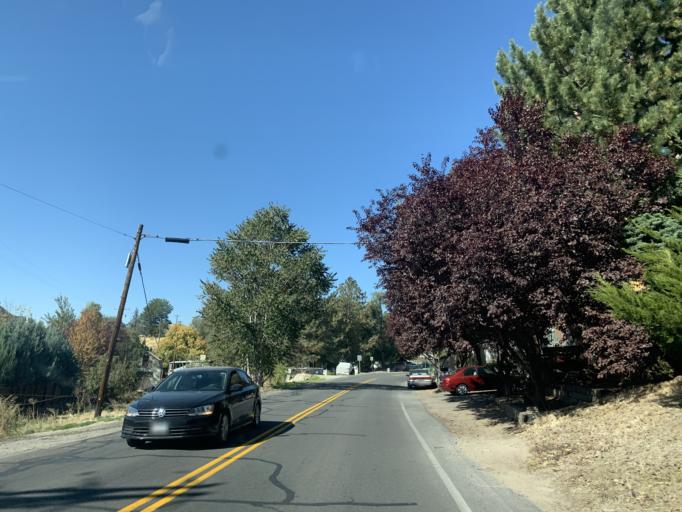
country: US
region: Utah
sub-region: Utah County
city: Orem
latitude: 40.2607
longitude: -111.6853
